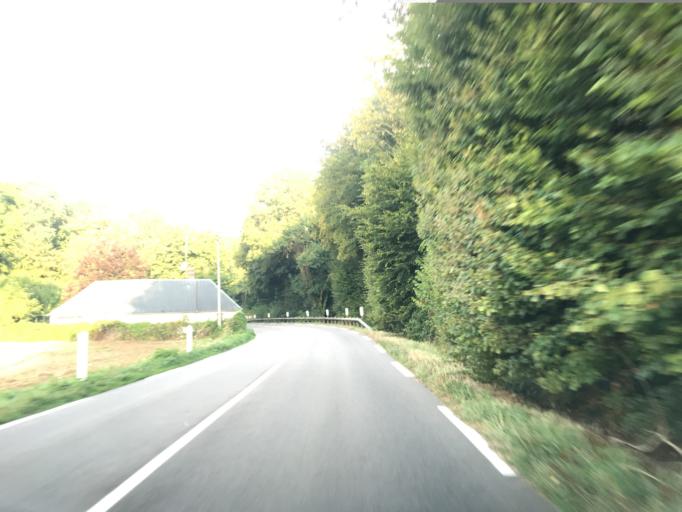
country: FR
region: Haute-Normandie
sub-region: Departement de l'Eure
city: Gravigny
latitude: 49.0650
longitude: 1.1999
